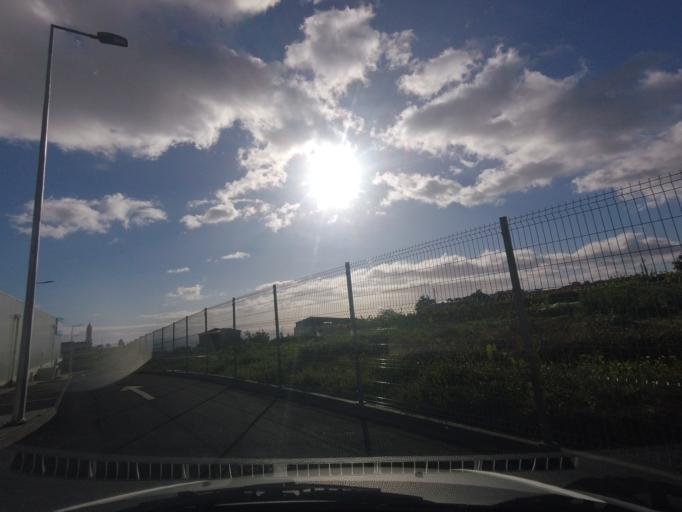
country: PT
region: Madeira
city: Camara de Lobos
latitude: 32.6547
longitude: -16.9432
